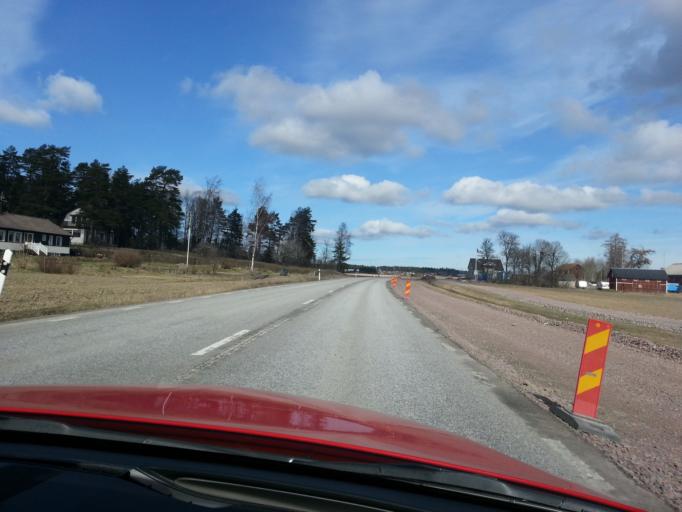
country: SE
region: Uppsala
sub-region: Osthammars Kommun
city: Gimo
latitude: 60.0451
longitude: 18.0453
